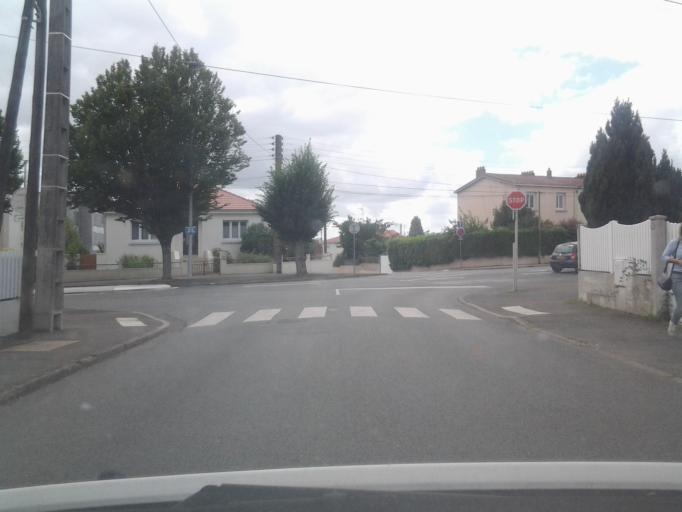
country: FR
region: Pays de la Loire
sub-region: Departement de la Vendee
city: La Roche-sur-Yon
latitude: 46.6595
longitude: -1.4362
